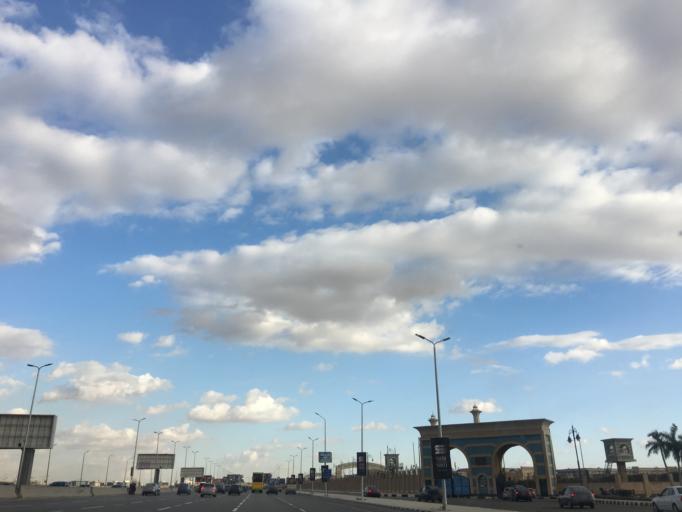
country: EG
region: Muhafazat al Qahirah
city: Cairo
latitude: 30.0204
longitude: 31.3780
